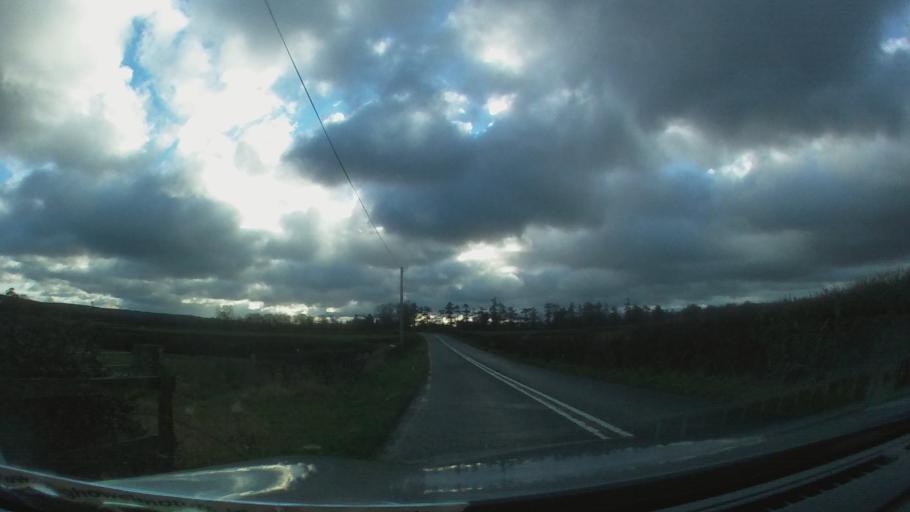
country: IE
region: Leinster
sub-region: Kilkenny
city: Thomastown
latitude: 52.5709
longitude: -7.1153
